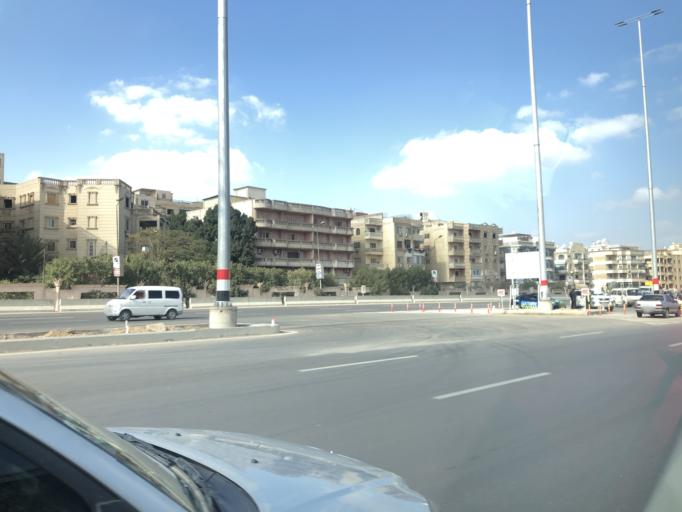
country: EG
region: Al Jizah
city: Al Jizah
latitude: 29.9737
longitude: 31.1100
